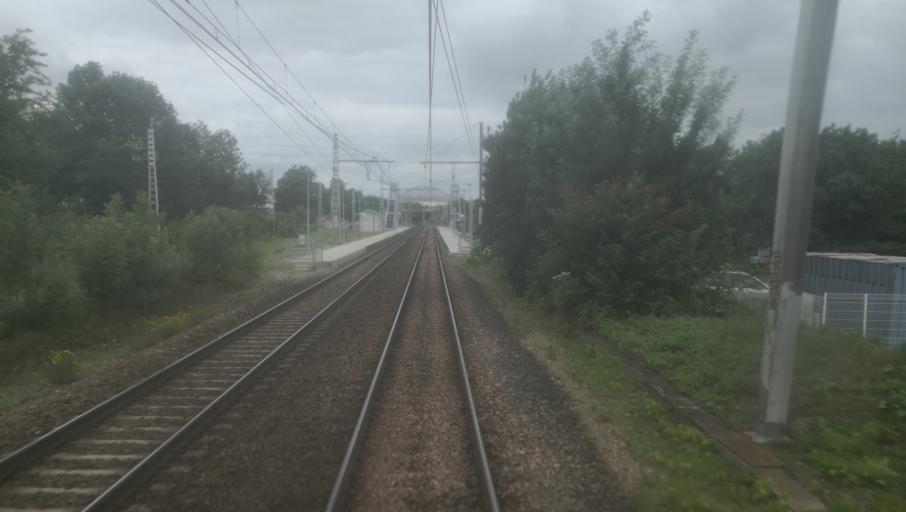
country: FR
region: Midi-Pyrenees
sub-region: Departement de la Haute-Garonne
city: Saint-Jory
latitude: 43.7373
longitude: 1.3724
